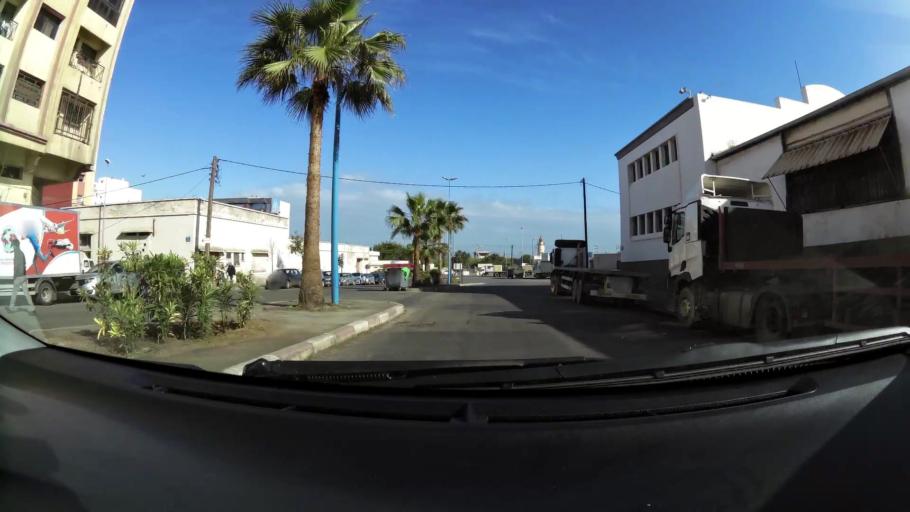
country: MA
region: Grand Casablanca
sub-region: Casablanca
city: Casablanca
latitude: 33.6030
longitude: -7.5789
